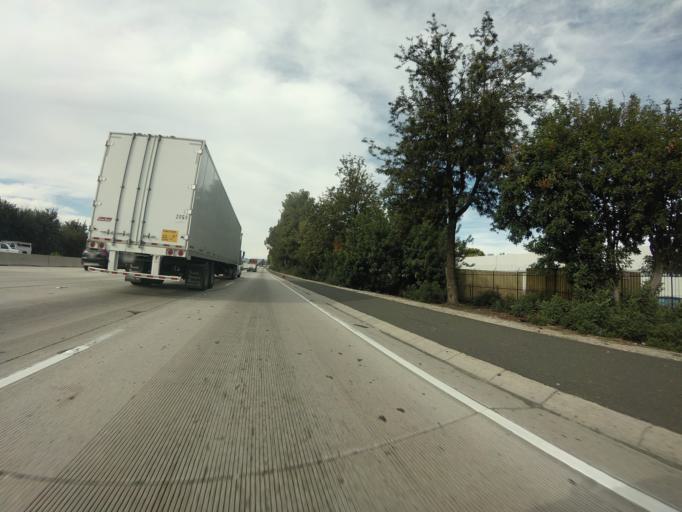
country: US
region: California
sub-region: Los Angeles County
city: Van Nuys
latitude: 34.1802
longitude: -118.4701
